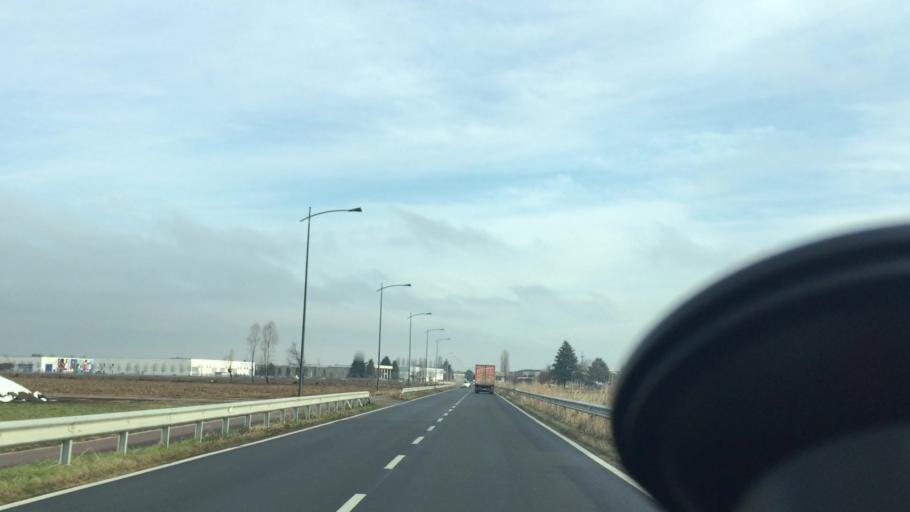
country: IT
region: Lombardy
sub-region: Provincia di Bergamo
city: Castel Rozzone
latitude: 45.5352
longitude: 9.6261
